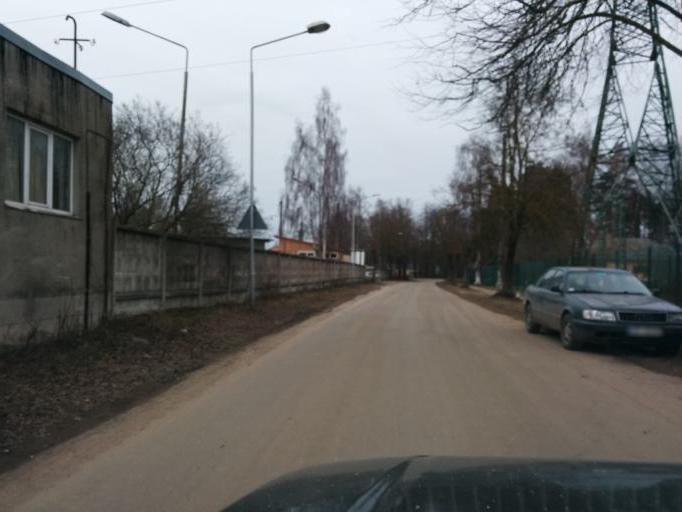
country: LV
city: Tireli
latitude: 56.9469
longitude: 23.6317
